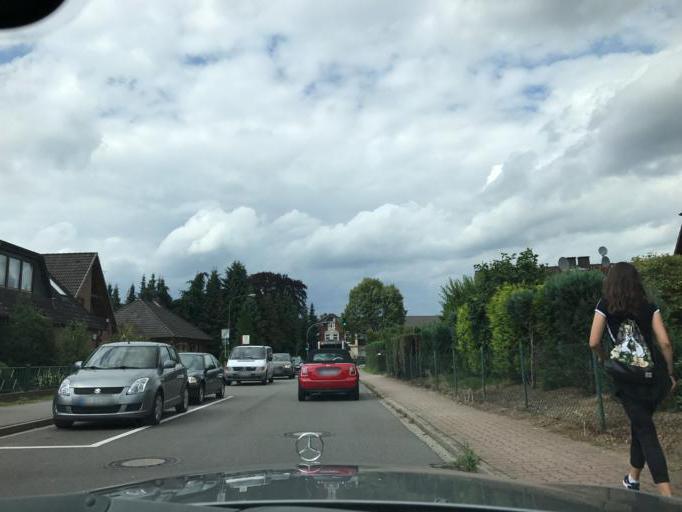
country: DE
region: Schleswig-Holstein
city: Oststeinbek
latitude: 53.5216
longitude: 10.1653
